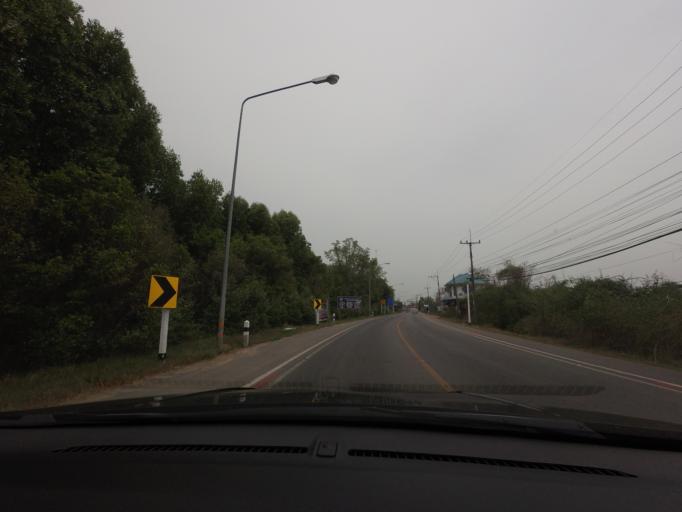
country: TH
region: Phetchaburi
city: Ban Laem
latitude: 13.2706
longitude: 99.9369
